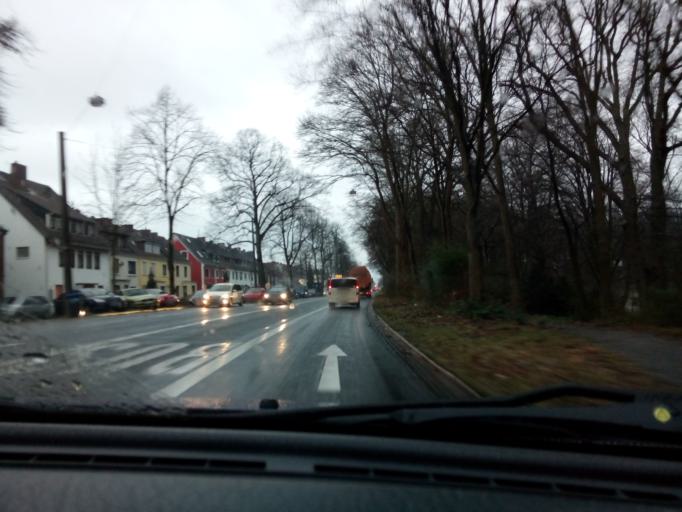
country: DE
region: Lower Saxony
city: Ritterhude
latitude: 53.1322
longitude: 8.7402
